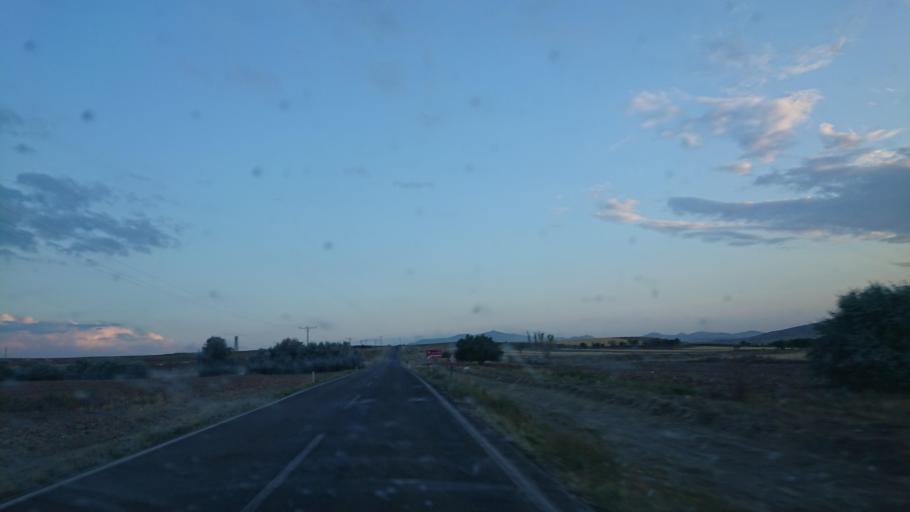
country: TR
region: Aksaray
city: Balci
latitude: 38.8058
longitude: 34.1308
